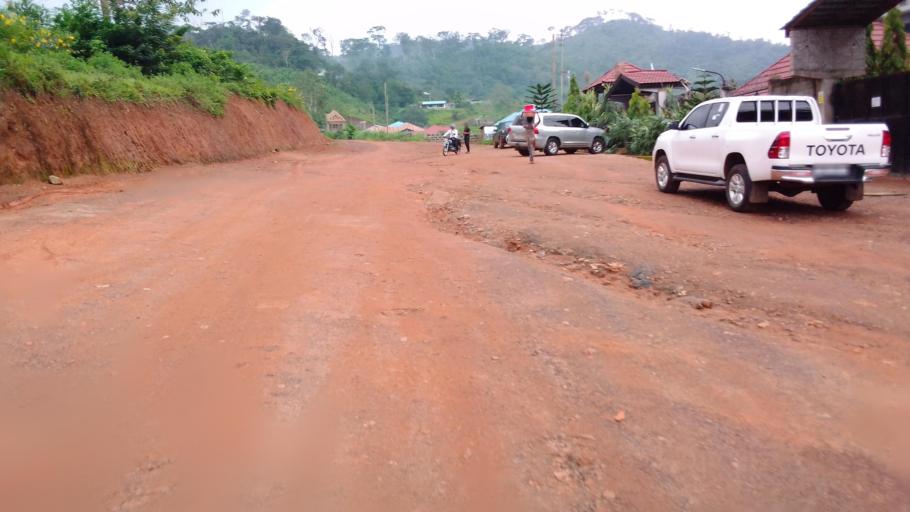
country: SL
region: Eastern Province
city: Kenema
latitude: 7.8893
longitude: -11.1942
